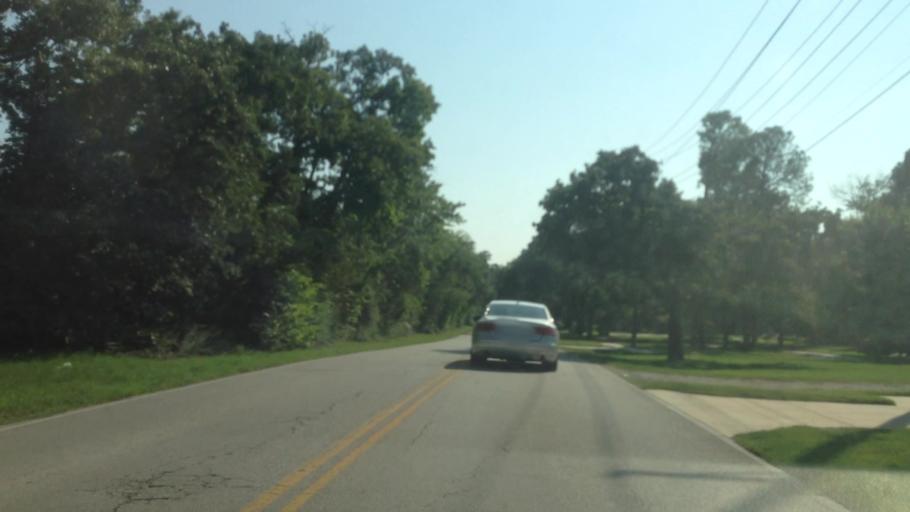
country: US
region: Texas
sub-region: Tarrant County
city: Colleyville
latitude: 32.8969
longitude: -97.1638
